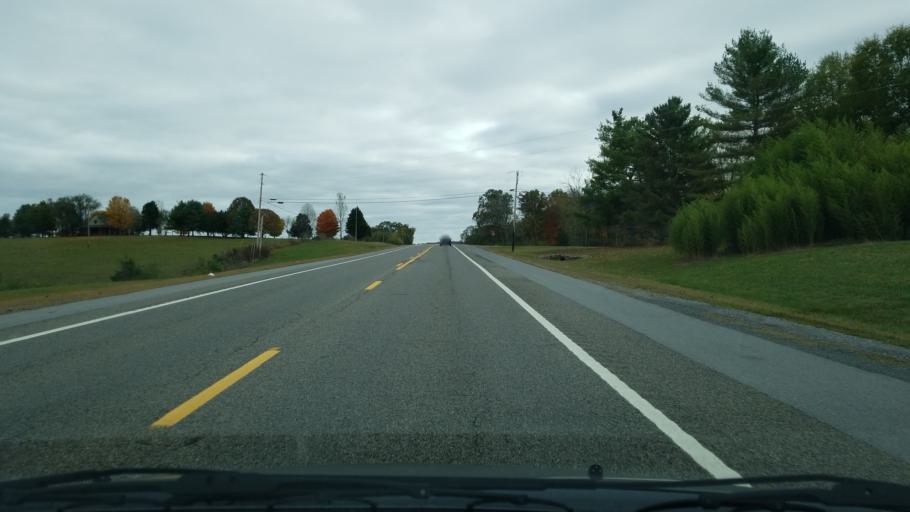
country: US
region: Tennessee
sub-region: Rhea County
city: Graysville
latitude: 35.3910
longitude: -85.0071
